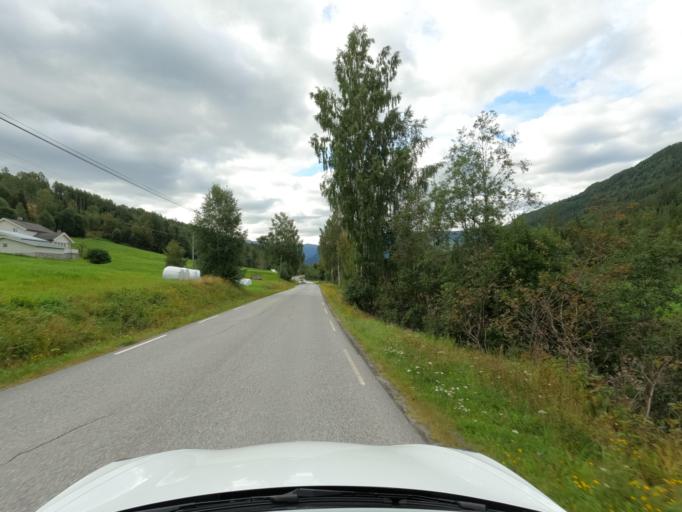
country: NO
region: Buskerud
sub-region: Nore og Uvdal
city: Rodberg
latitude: 60.0134
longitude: 8.8375
